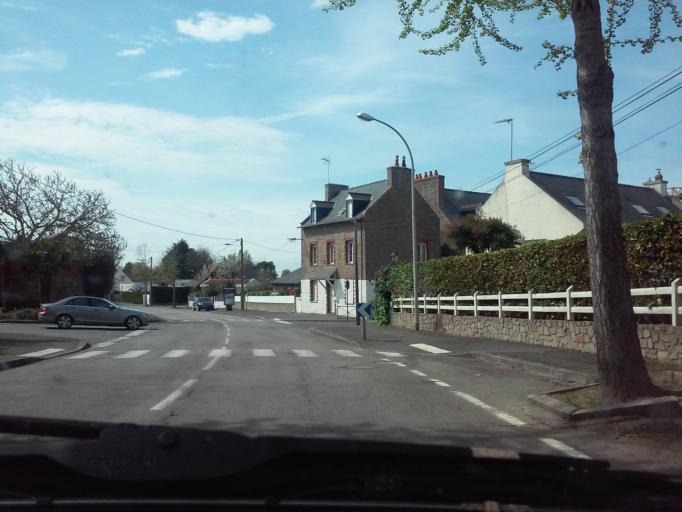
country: FR
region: Brittany
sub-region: Departement d'Ille-et-Vilaine
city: Dinard
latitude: 48.6338
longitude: -2.0672
